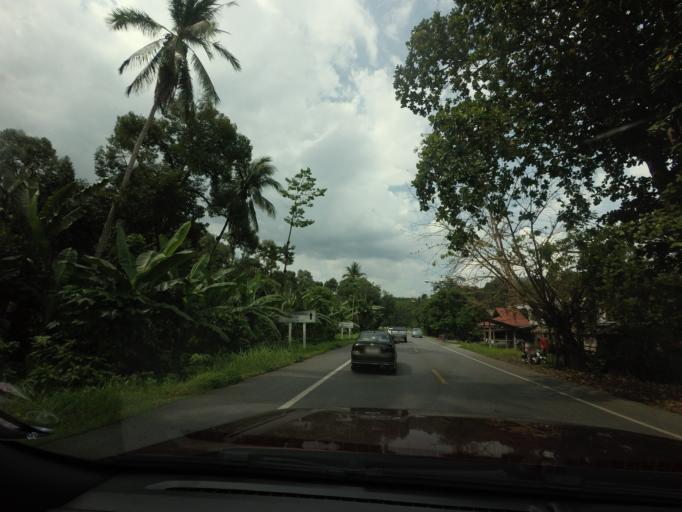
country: TH
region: Yala
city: Ban Nang Sata
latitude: 6.2763
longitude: 101.2872
